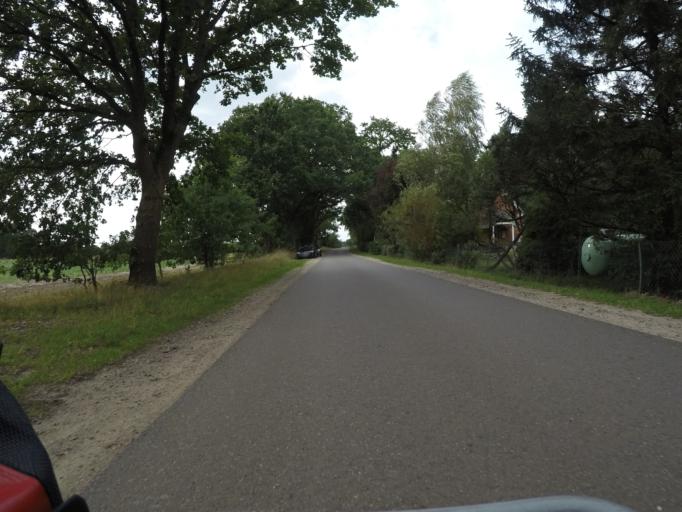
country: DE
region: Lower Saxony
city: Bardowick
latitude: 53.3059
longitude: 10.4036
